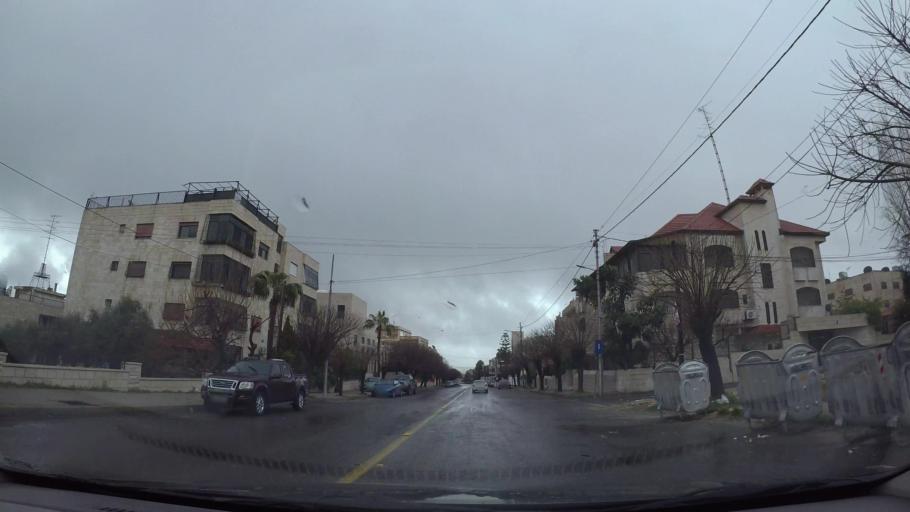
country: JO
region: Amman
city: Wadi as Sir
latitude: 31.9688
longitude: 35.8525
